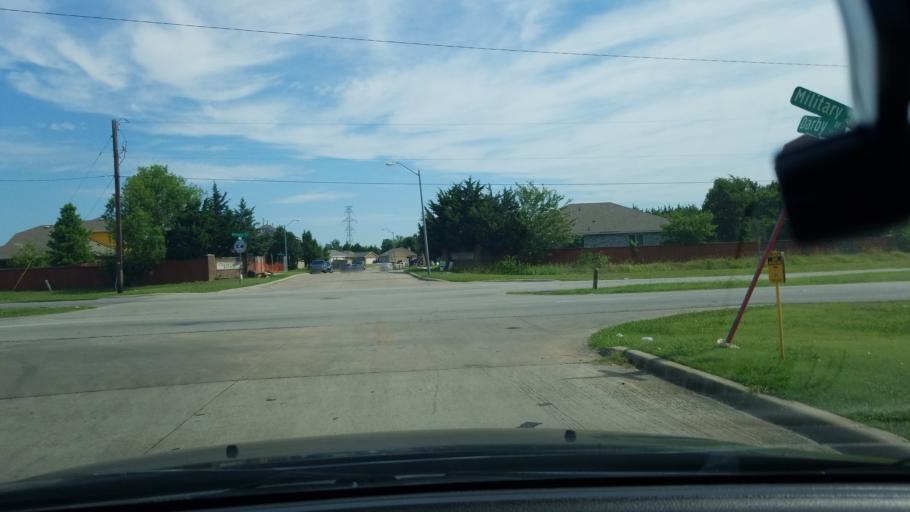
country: US
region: Texas
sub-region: Dallas County
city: Balch Springs
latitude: 32.7682
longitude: -96.6713
